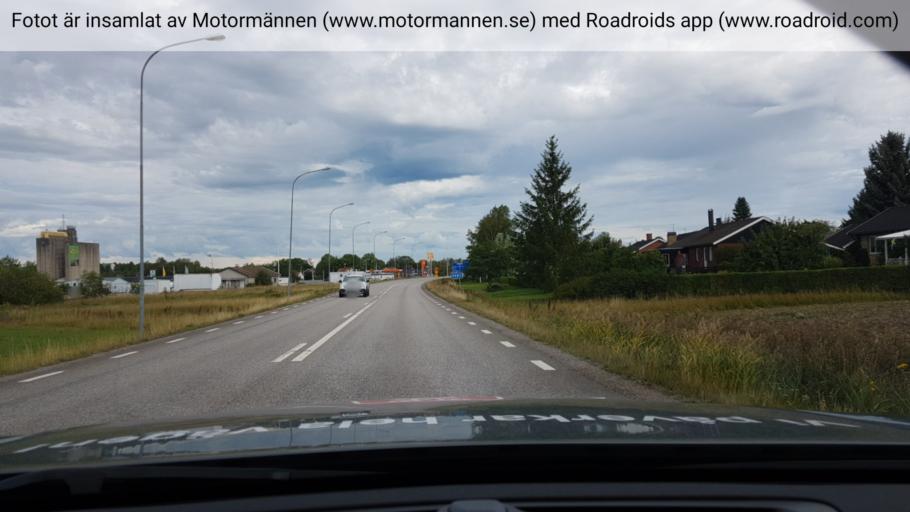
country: SE
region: Uppsala
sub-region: Heby Kommun
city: Heby
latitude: 59.9327
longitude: 16.8709
